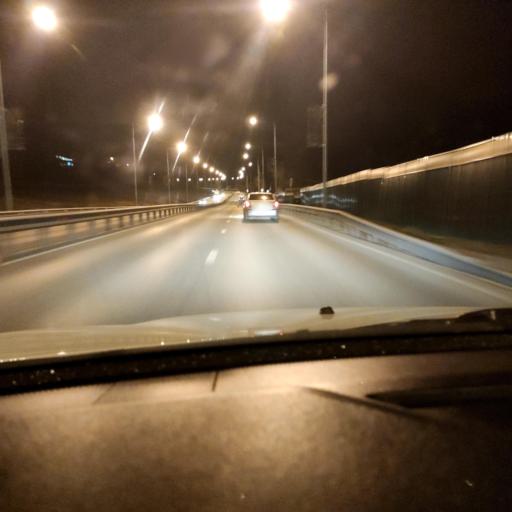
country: RU
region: Samara
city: Volzhskiy
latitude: 53.3772
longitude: 50.1710
